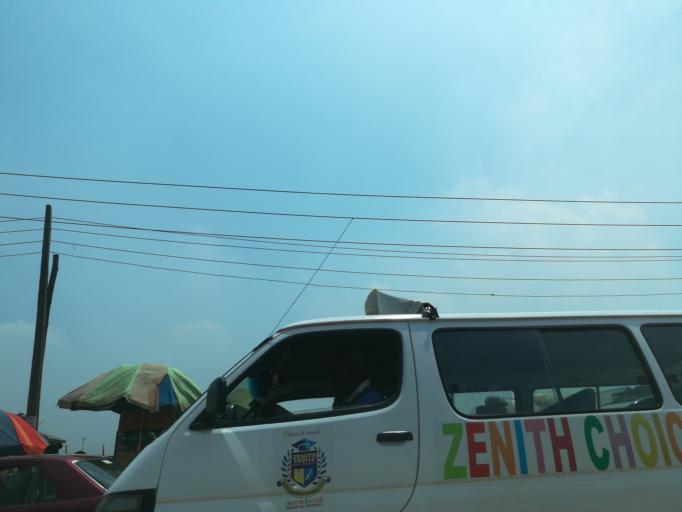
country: NG
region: Lagos
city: Ikorodu
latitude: 6.6269
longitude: 3.4840
